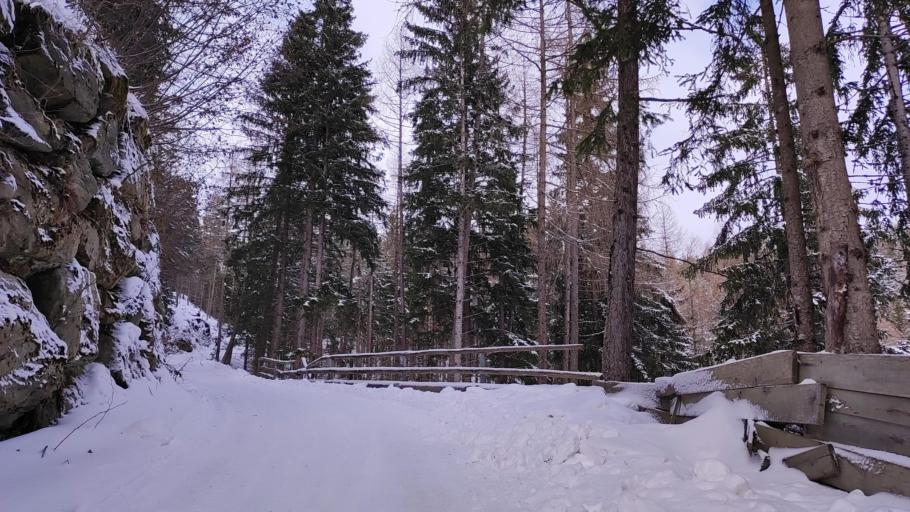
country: AT
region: Tyrol
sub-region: Politischer Bezirk Imst
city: Umhausen
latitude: 47.1006
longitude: 10.9360
